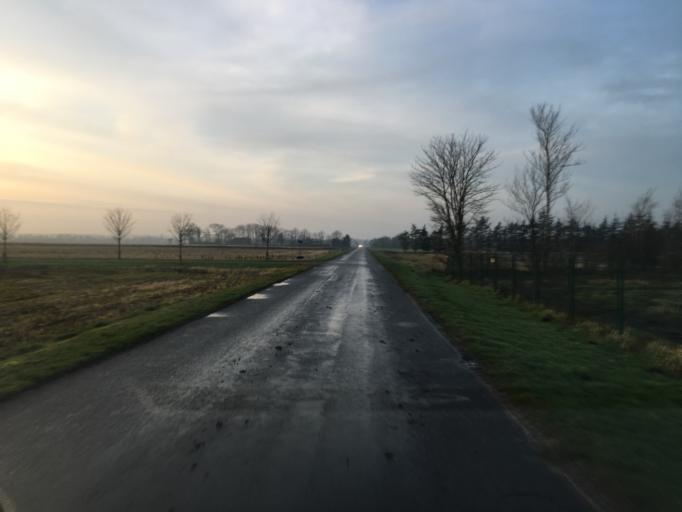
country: DK
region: South Denmark
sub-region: Tonder Kommune
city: Logumkloster
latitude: 55.1109
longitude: 8.9863
